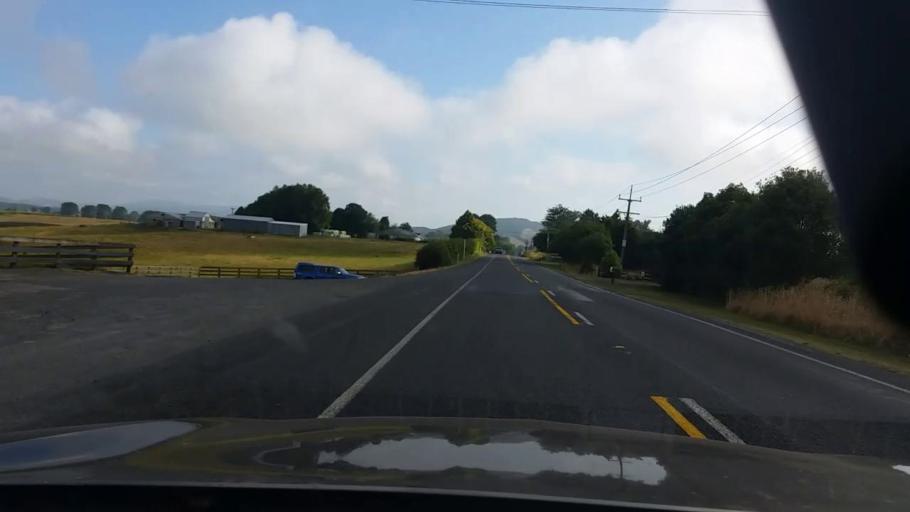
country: NZ
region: Waikato
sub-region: Hamilton City
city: Hamilton
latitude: -37.6138
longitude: 175.3448
